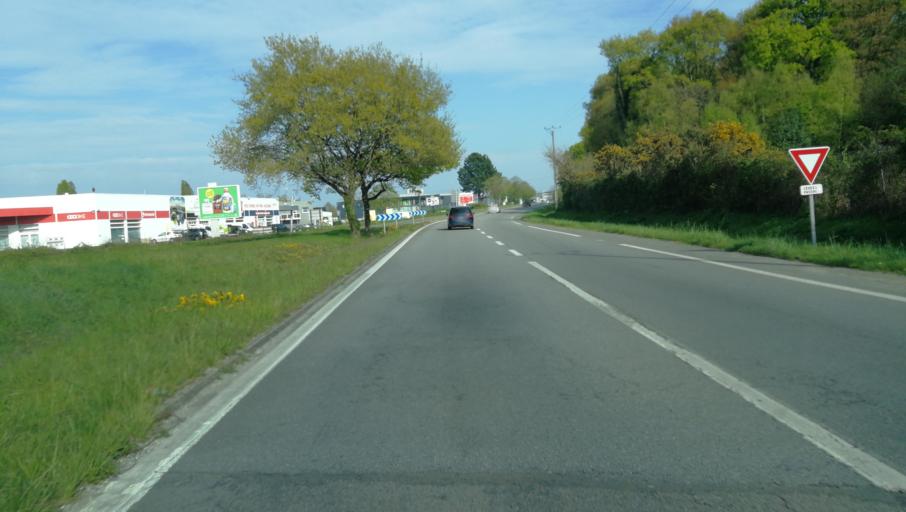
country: FR
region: Pays de la Loire
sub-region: Departement de la Loire-Atlantique
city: Orvault
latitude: 47.2562
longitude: -1.6368
